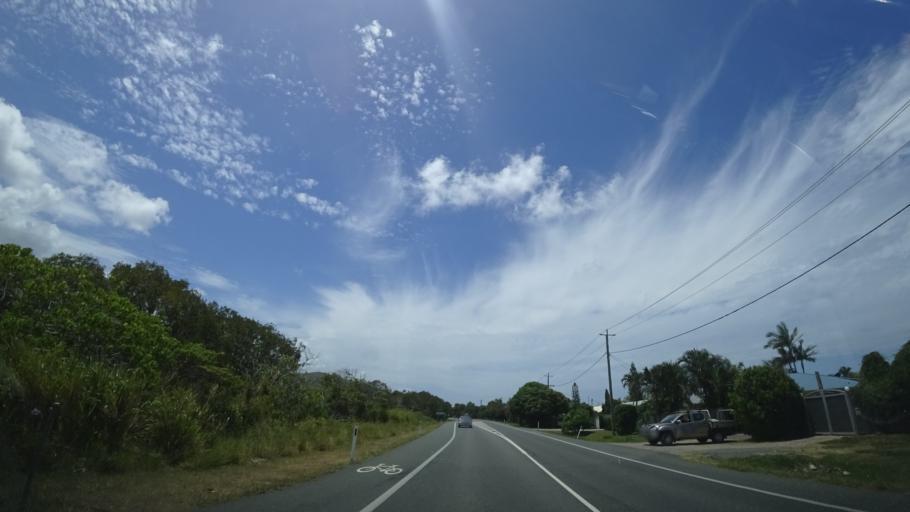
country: AU
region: Queensland
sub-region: Sunshine Coast
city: Coolum Beach
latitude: -26.5825
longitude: 153.0931
